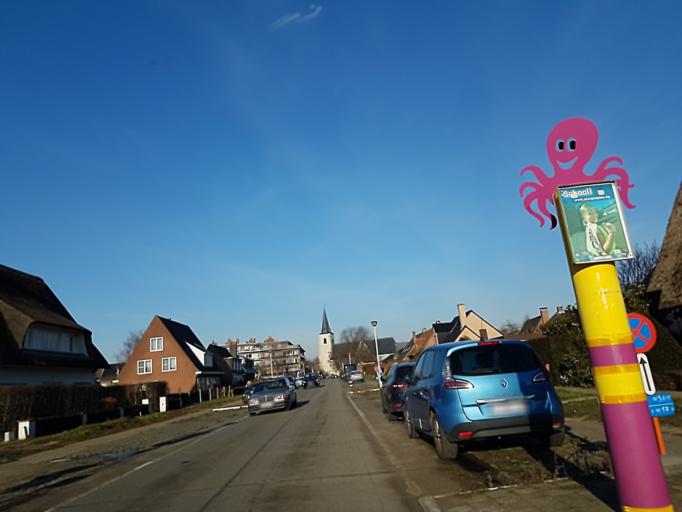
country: BE
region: Flanders
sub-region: Provincie Antwerpen
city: Hove
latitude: 51.1518
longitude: 4.4716
